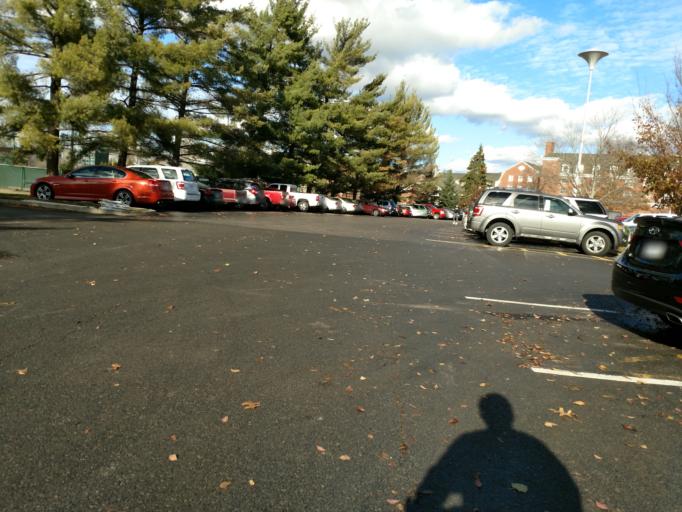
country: US
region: Ohio
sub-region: Athens County
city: Athens
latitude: 39.3233
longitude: -82.1070
